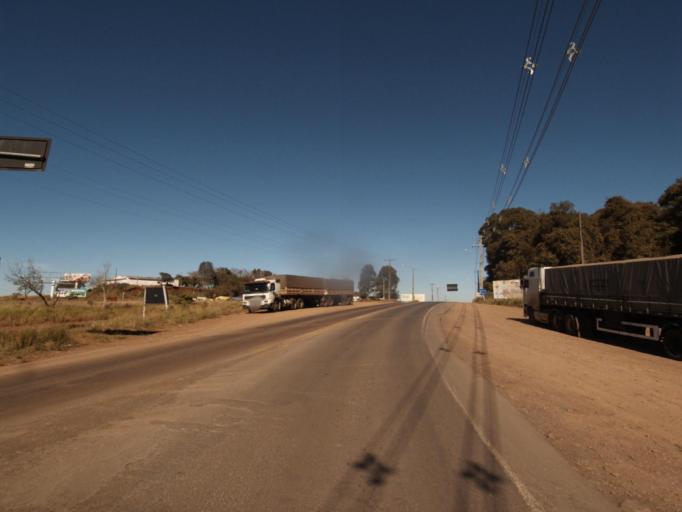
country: AR
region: Misiones
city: Bernardo de Irigoyen
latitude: -26.7618
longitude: -53.5004
